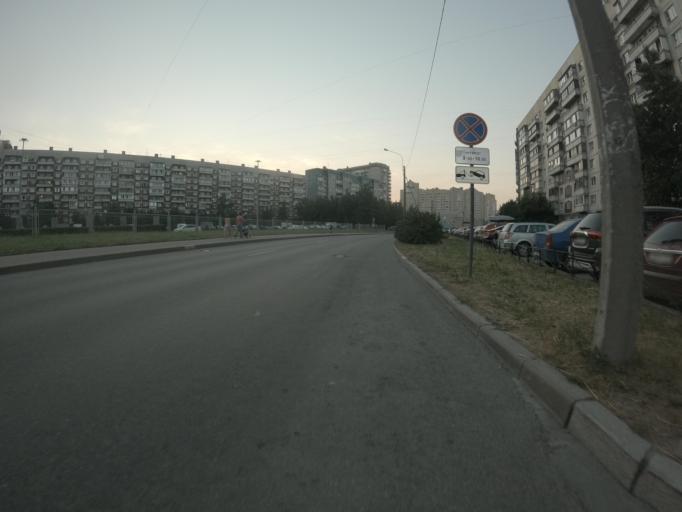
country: RU
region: St.-Petersburg
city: Krasnogvargeisky
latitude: 59.9212
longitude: 30.4544
